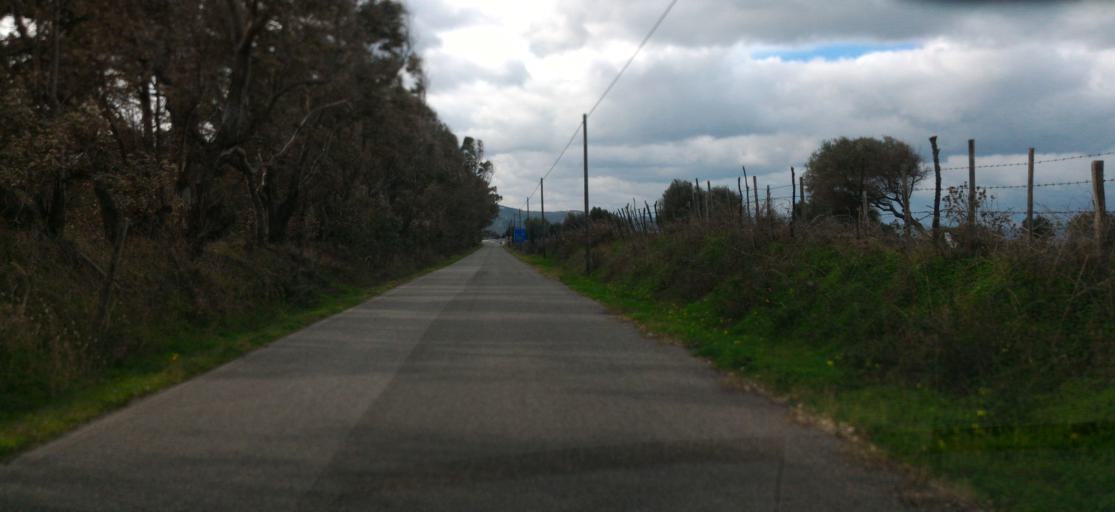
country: IT
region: Calabria
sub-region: Provincia di Crotone
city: Ciro Marina
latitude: 39.4009
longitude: 17.1204
